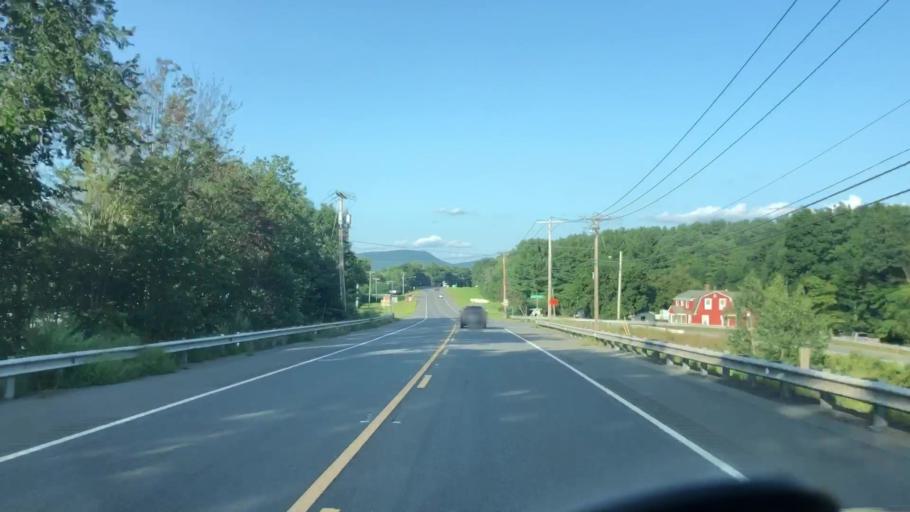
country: US
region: Massachusetts
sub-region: Franklin County
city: Gill
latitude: 42.6736
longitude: -72.5036
